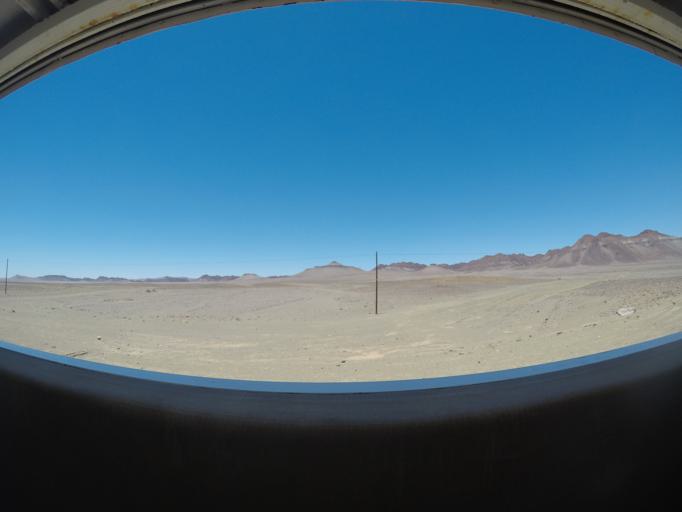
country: ZA
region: Northern Cape
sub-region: Namakwa District Municipality
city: Port Nolloth
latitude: -28.6020
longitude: 17.4854
